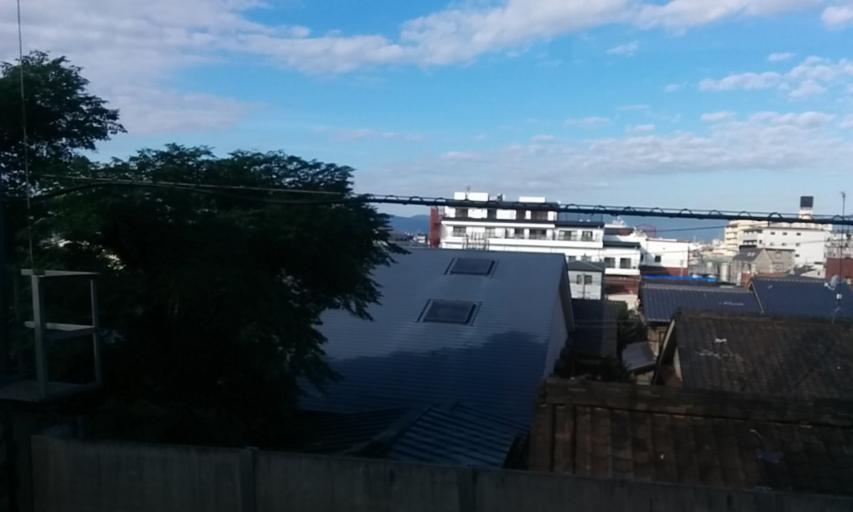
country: JP
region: Kyoto
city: Uji
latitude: 34.9306
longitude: 135.7651
